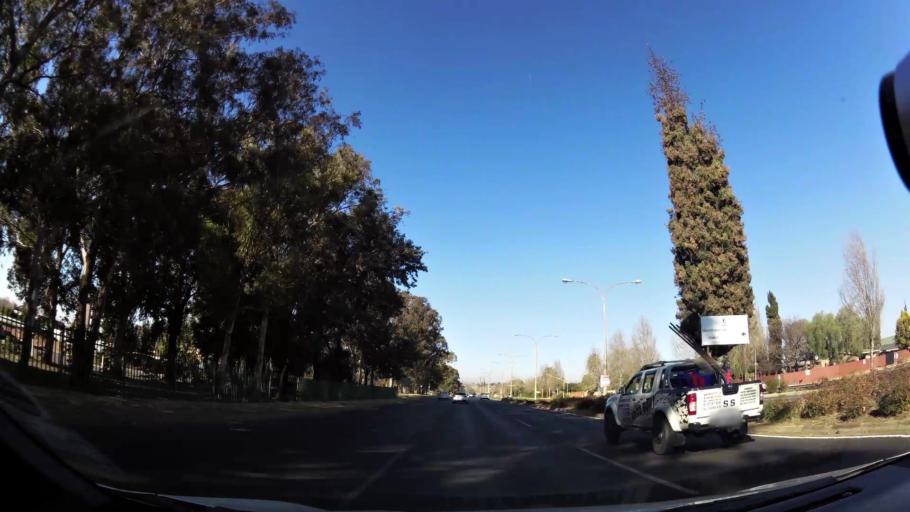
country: ZA
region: Gauteng
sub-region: Ekurhuleni Metropolitan Municipality
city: Germiston
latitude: -26.2878
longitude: 28.1203
